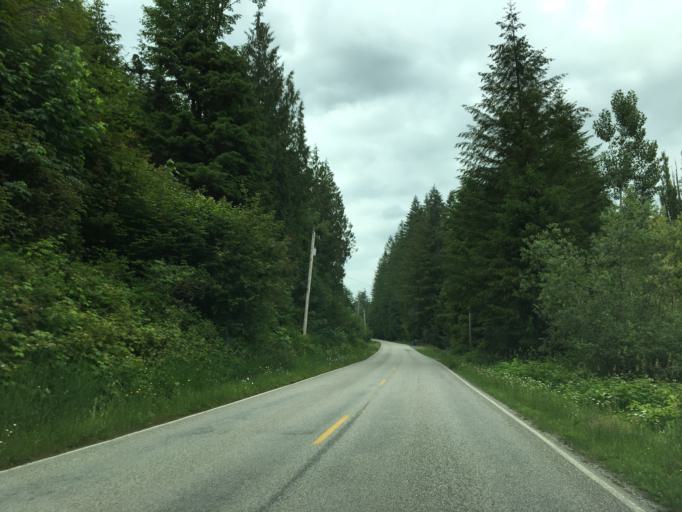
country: US
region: Washington
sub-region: Whatcom County
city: Peaceful Valley
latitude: 48.9544
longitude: -122.0739
